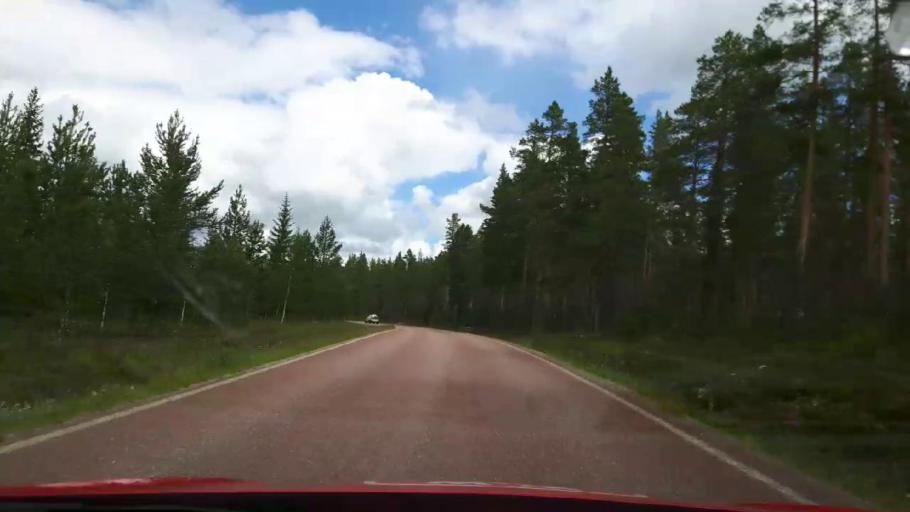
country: NO
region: Hedmark
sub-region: Trysil
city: Innbygda
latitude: 61.9108
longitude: 13.0057
